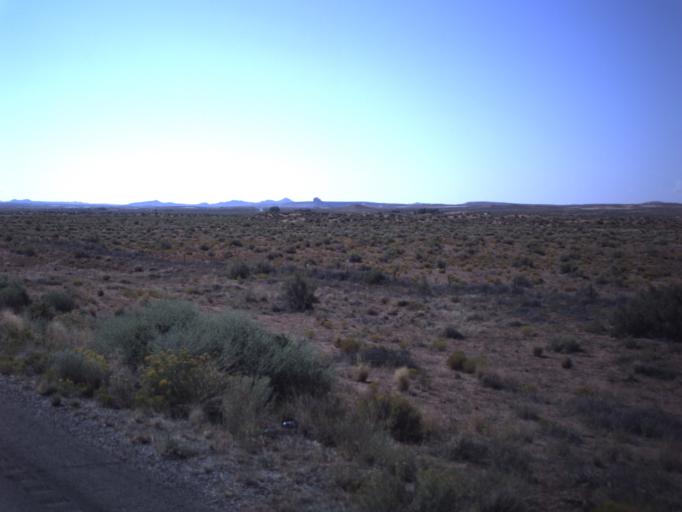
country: US
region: Utah
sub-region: San Juan County
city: Blanding
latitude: 37.1255
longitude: -109.5469
